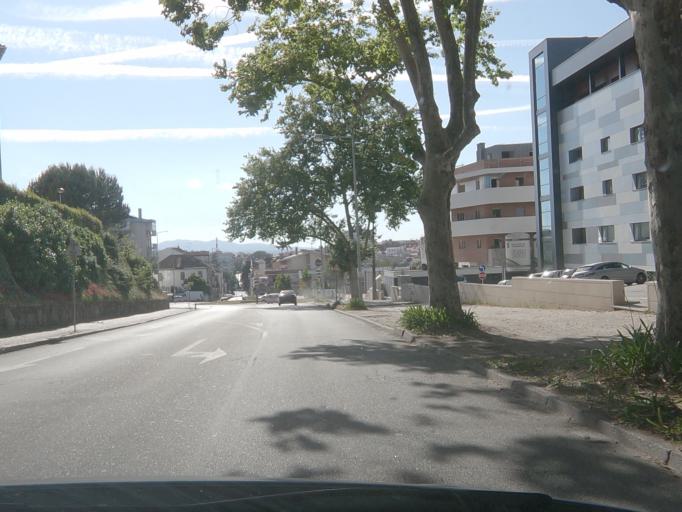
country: PT
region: Viseu
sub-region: Viseu
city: Viseu
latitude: 40.6563
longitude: -7.9046
